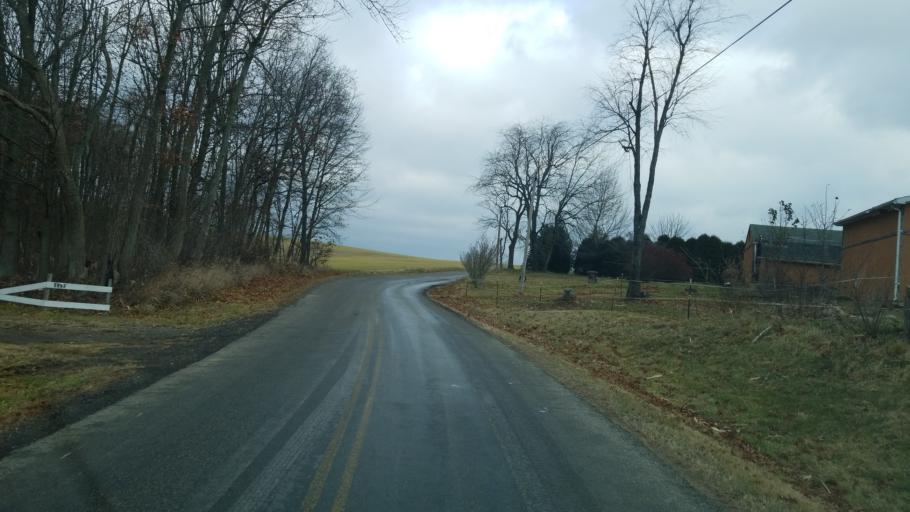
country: US
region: Ohio
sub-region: Holmes County
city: Millersburg
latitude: 40.5789
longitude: -81.9645
